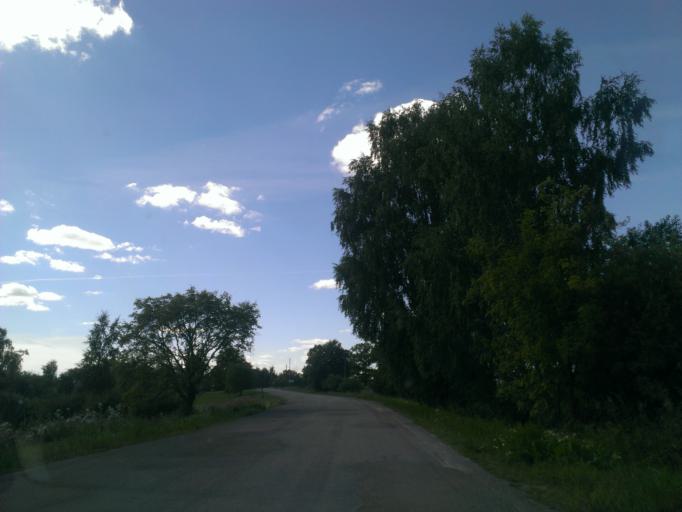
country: LV
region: Malpils
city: Malpils
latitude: 57.0136
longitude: 24.9777
